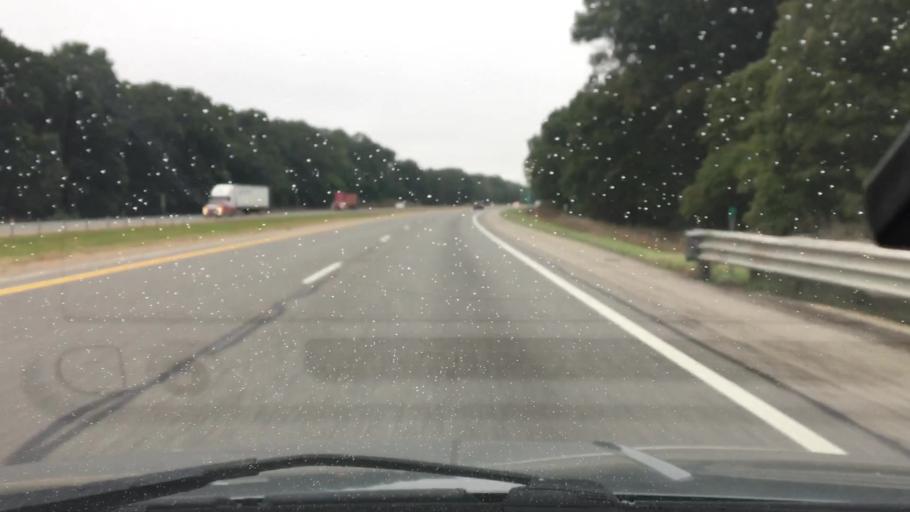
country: US
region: Michigan
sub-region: Van Buren County
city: Mattawan
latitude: 42.2236
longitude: -85.7383
